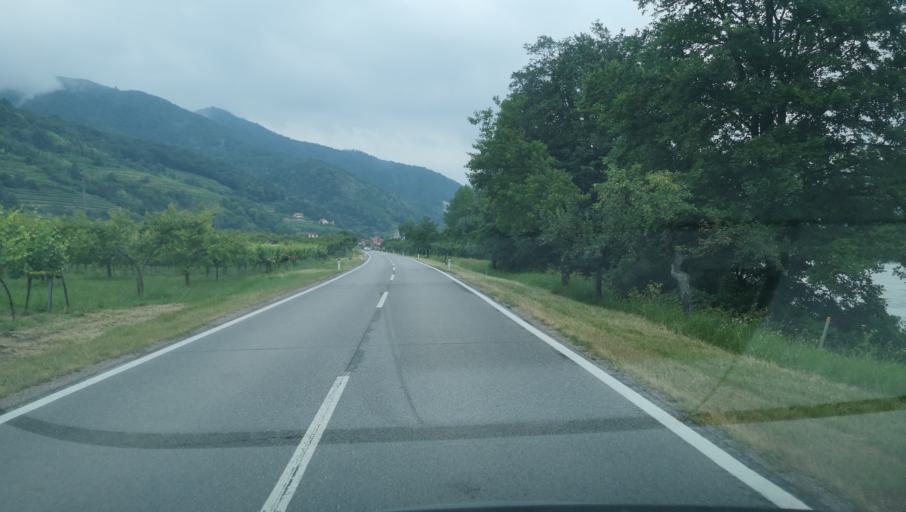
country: AT
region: Lower Austria
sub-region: Politischer Bezirk Krems
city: Spitz
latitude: 48.3304
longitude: 15.4059
